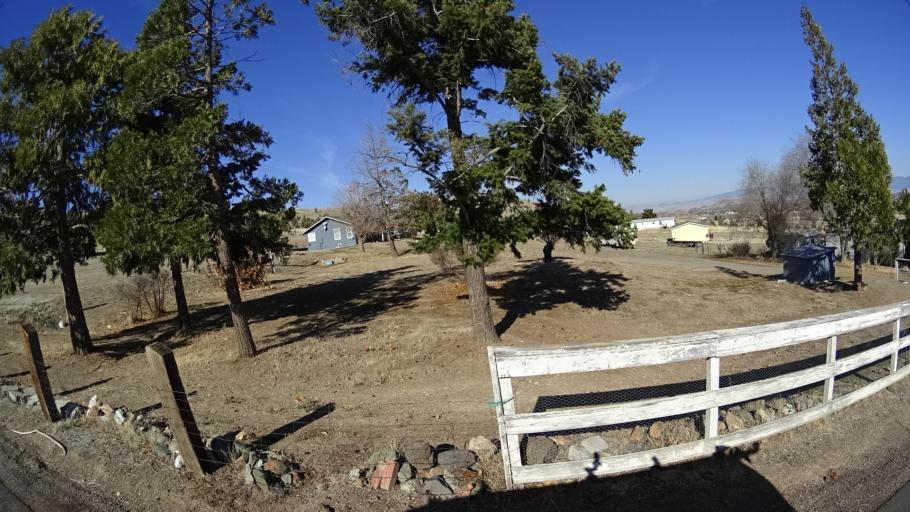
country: US
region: California
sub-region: Siskiyou County
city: Montague
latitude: 41.6327
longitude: -122.5388
